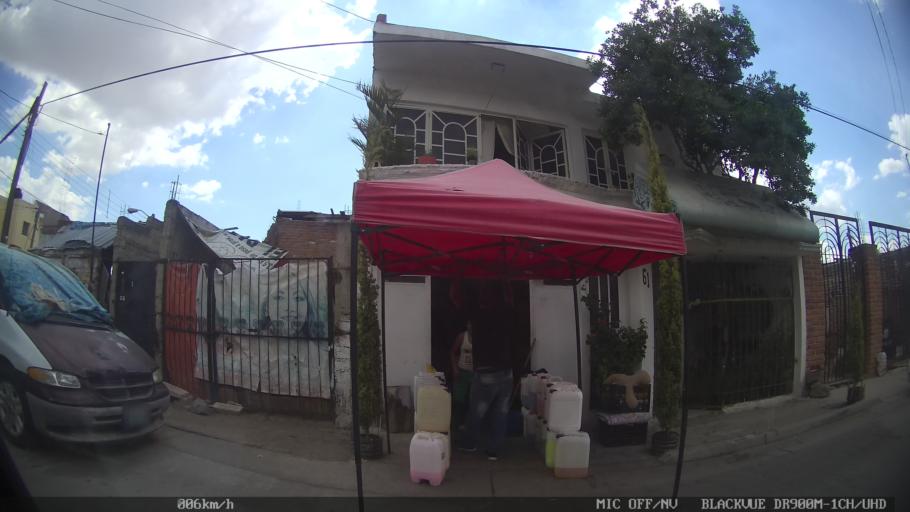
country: MX
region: Jalisco
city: Tlaquepaque
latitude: 20.6803
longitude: -103.2640
